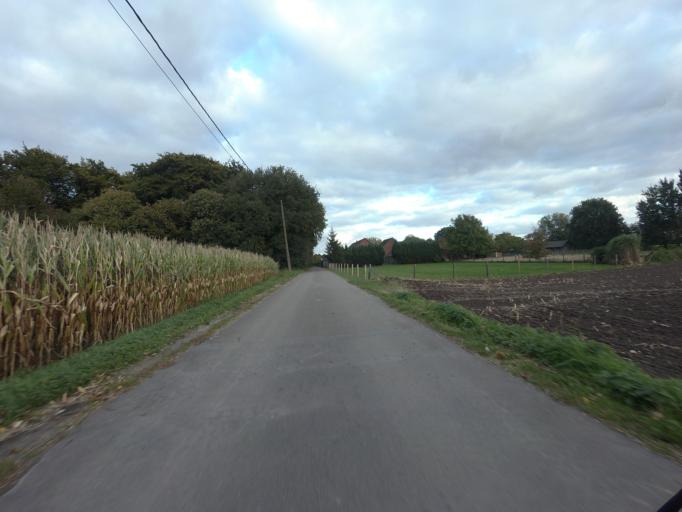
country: BE
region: Flanders
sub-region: Provincie Antwerpen
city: Willebroek
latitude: 51.0523
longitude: 4.3967
